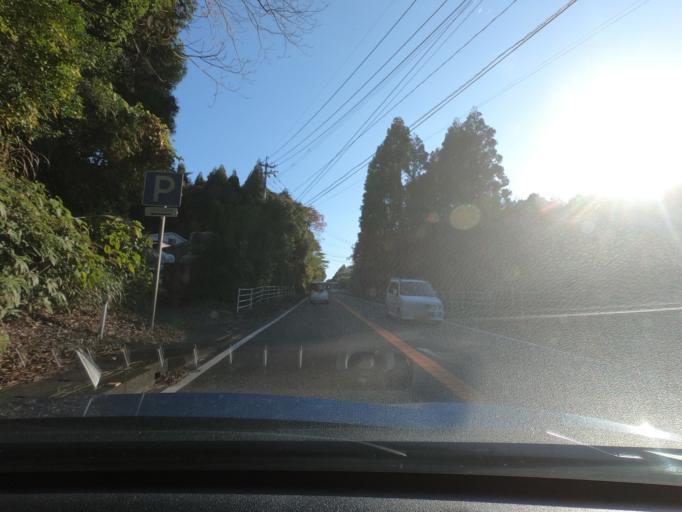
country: JP
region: Kagoshima
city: Akune
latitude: 32.0514
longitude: 130.2209
